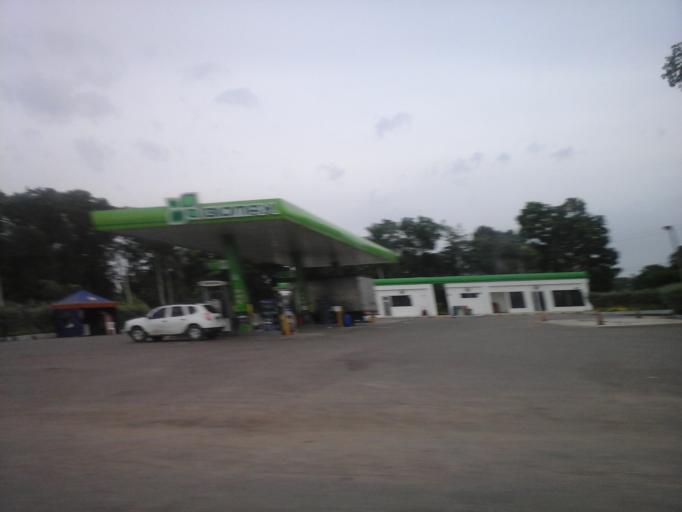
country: CO
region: Bolivar
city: San Pablo
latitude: 10.1366
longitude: -75.2704
